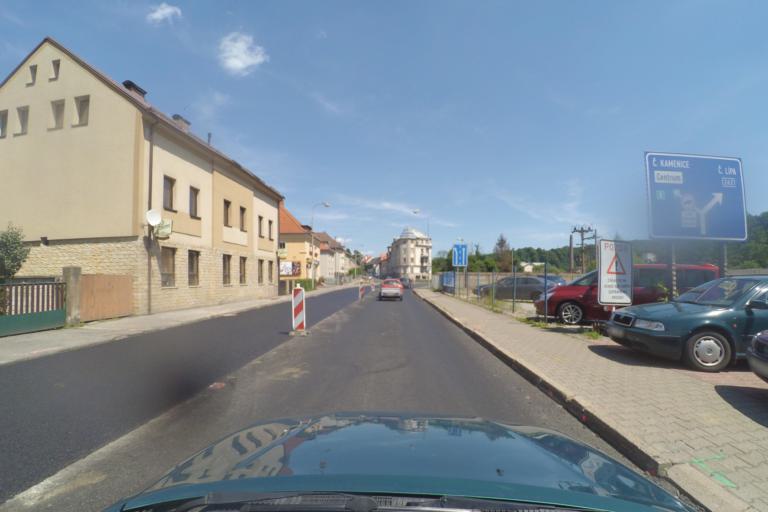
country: CZ
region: Ustecky
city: Benesov nad Ploucnici
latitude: 50.7410
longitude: 14.3024
